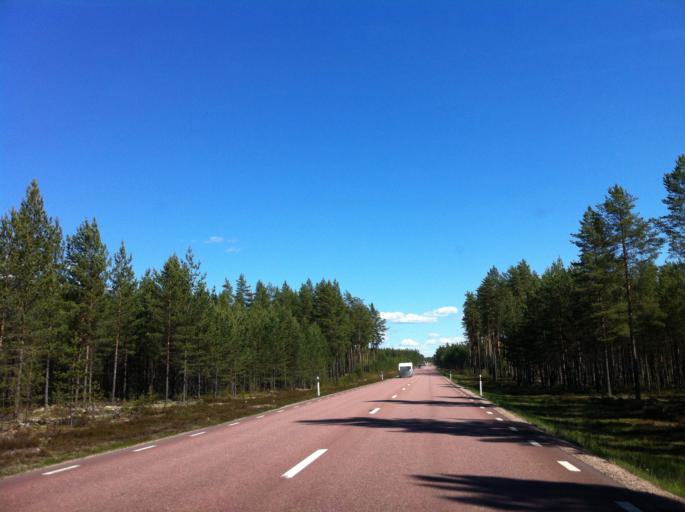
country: SE
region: Dalarna
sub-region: Mora Kommun
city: Mora
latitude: 60.9527
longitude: 14.7336
